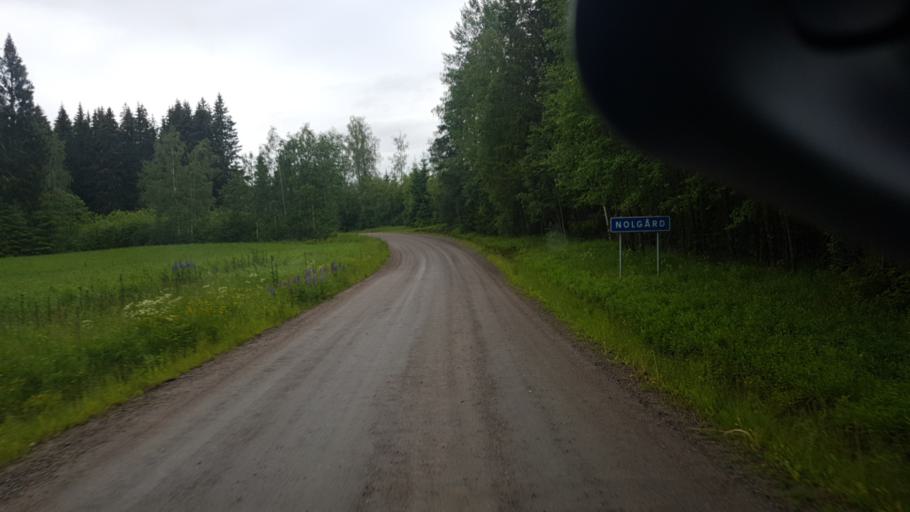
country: NO
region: Hedmark
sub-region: Eidskog
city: Skotterud
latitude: 59.7332
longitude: 12.0962
